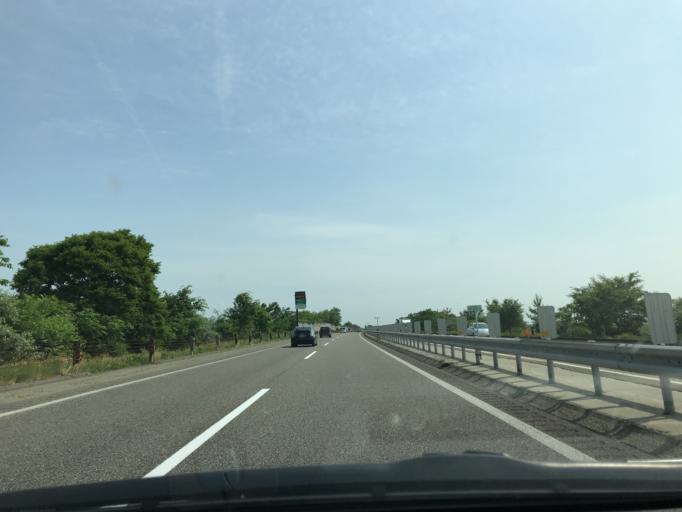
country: JP
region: Niigata
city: Sanjo
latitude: 37.5949
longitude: 138.8966
